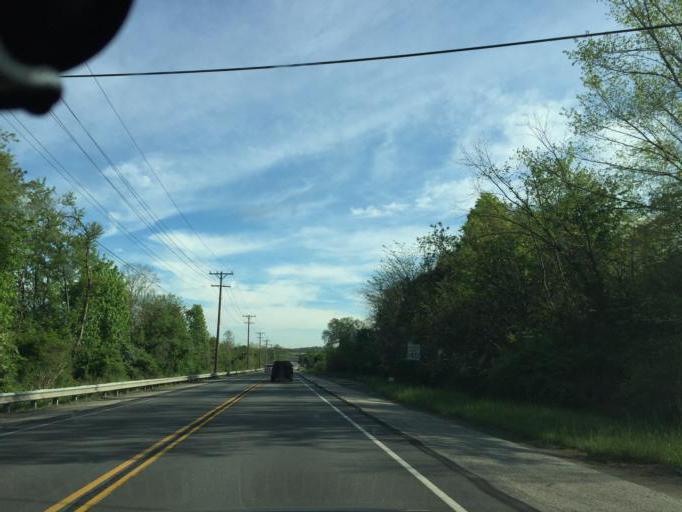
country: US
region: Pennsylvania
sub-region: Westmoreland County
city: Lawson Heights
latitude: 40.2992
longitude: -79.3940
